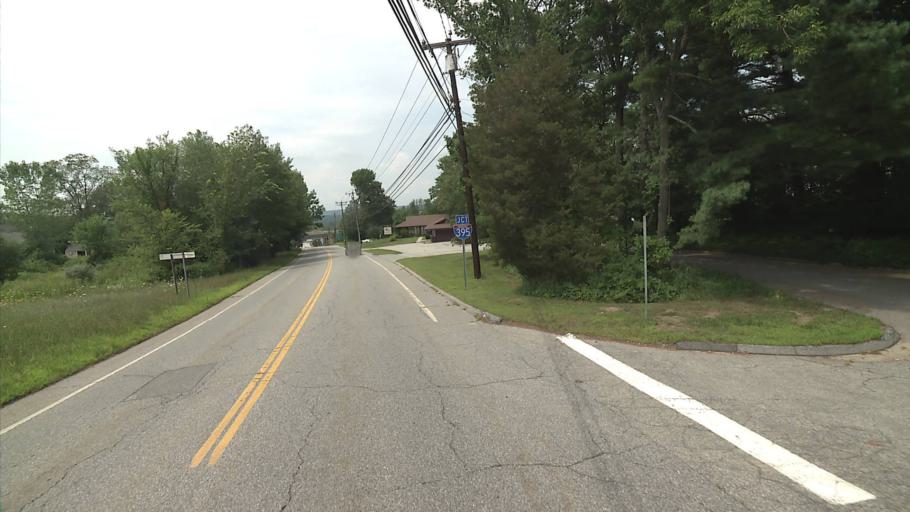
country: US
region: Connecticut
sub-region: Windham County
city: Danielson
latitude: 41.8094
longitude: -71.8693
